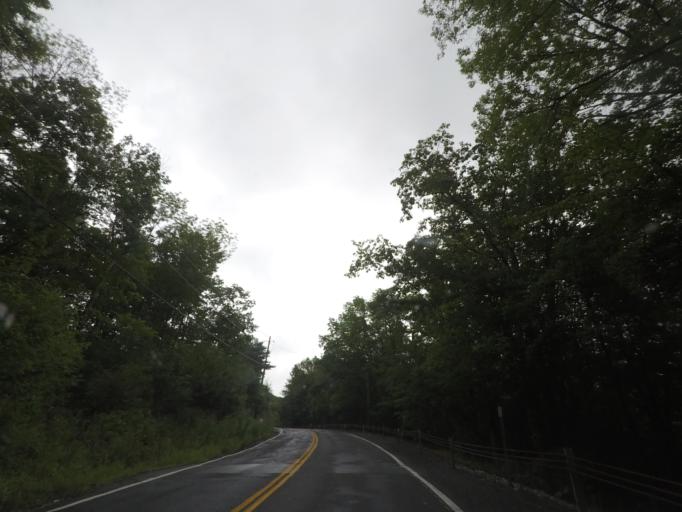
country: US
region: New York
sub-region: Rensselaer County
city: Averill Park
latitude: 42.5773
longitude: -73.4703
